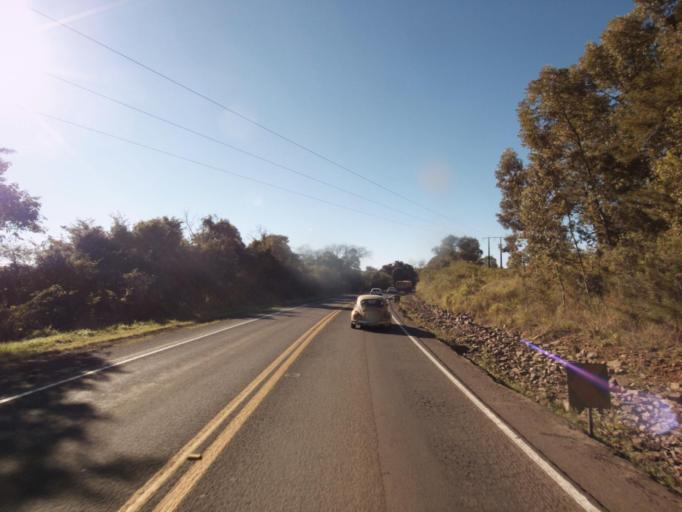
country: AR
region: Misiones
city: Bernardo de Irigoyen
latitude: -26.5692
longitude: -53.5109
